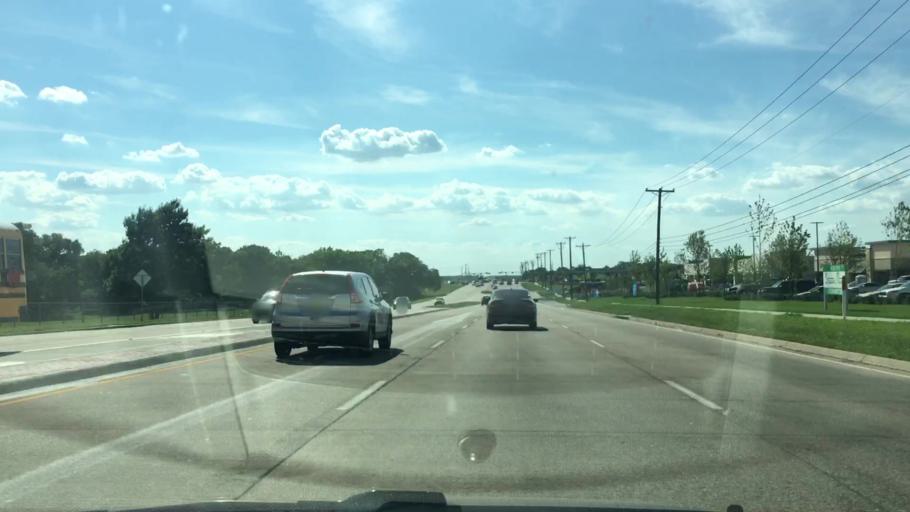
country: US
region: Texas
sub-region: Collin County
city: McKinney
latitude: 33.2172
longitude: -96.6560
